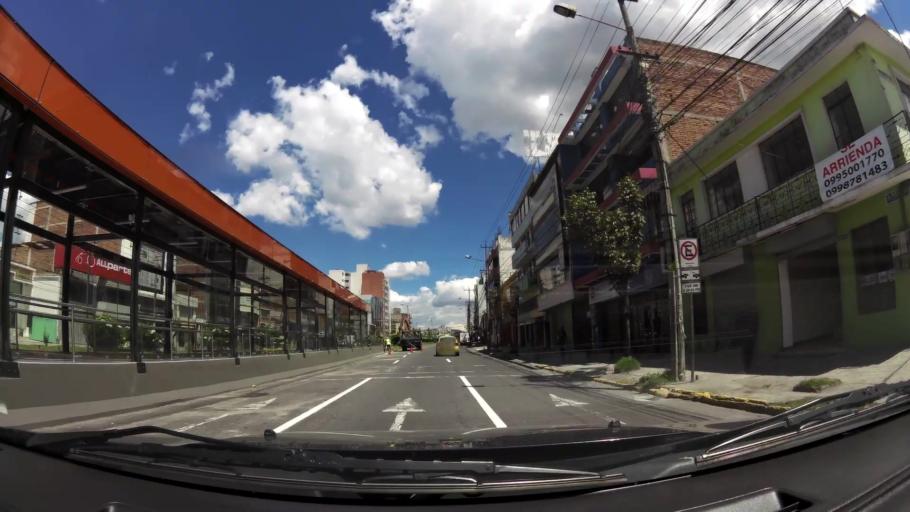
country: EC
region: Pichincha
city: Quito
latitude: -0.1789
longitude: -78.4890
